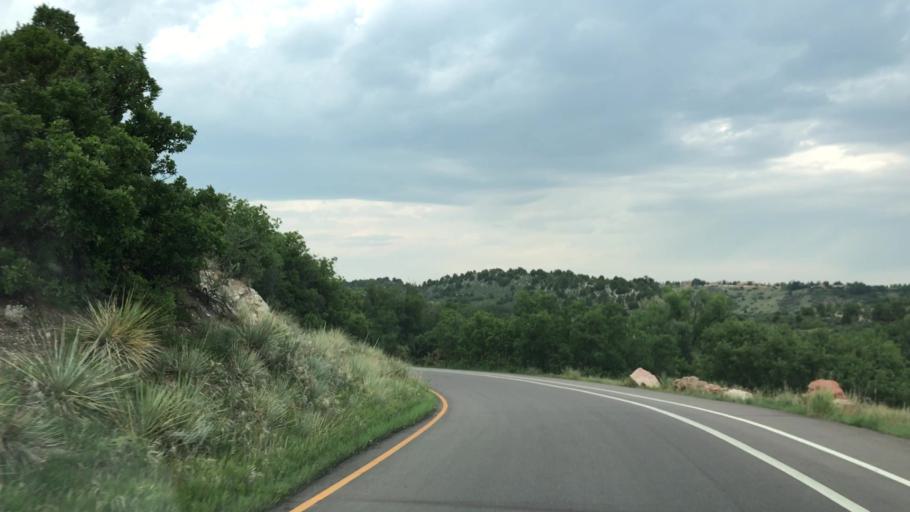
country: US
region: Colorado
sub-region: El Paso County
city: Manitou Springs
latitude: 38.8731
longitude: -104.8785
